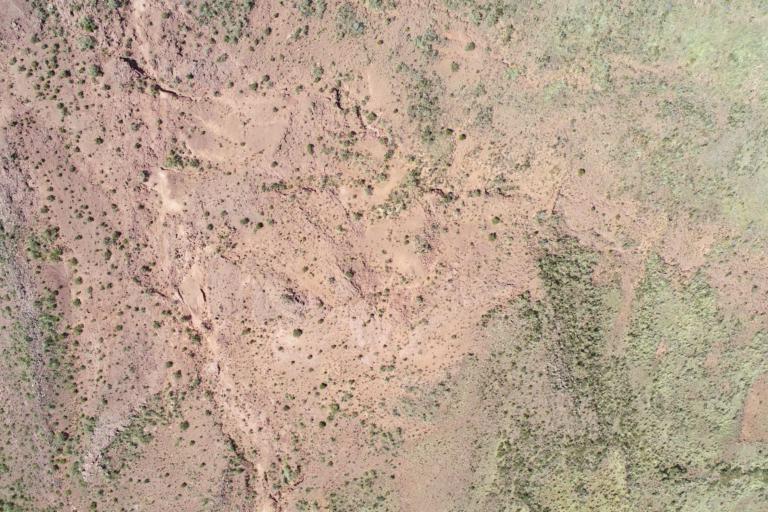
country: BO
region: La Paz
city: Tiahuanaco
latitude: -16.6038
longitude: -68.7563
